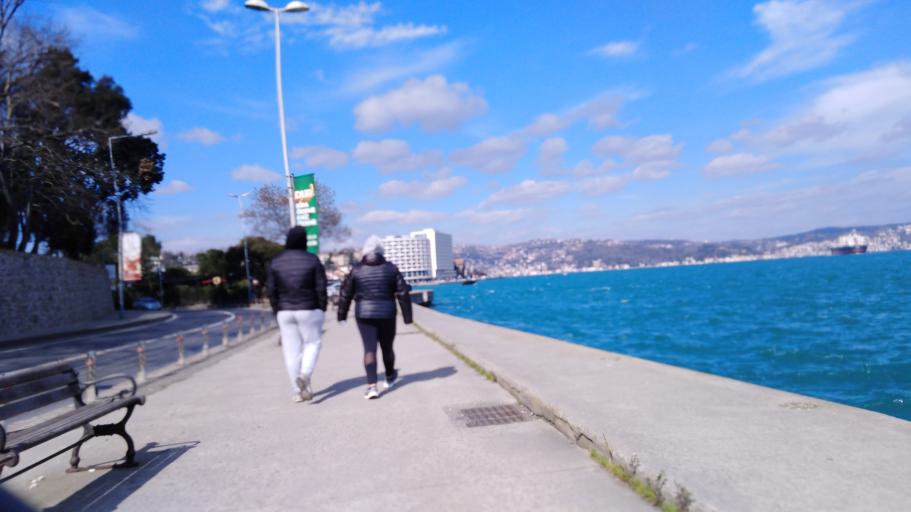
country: TR
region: Istanbul
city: Sisli
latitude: 41.1350
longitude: 29.0616
